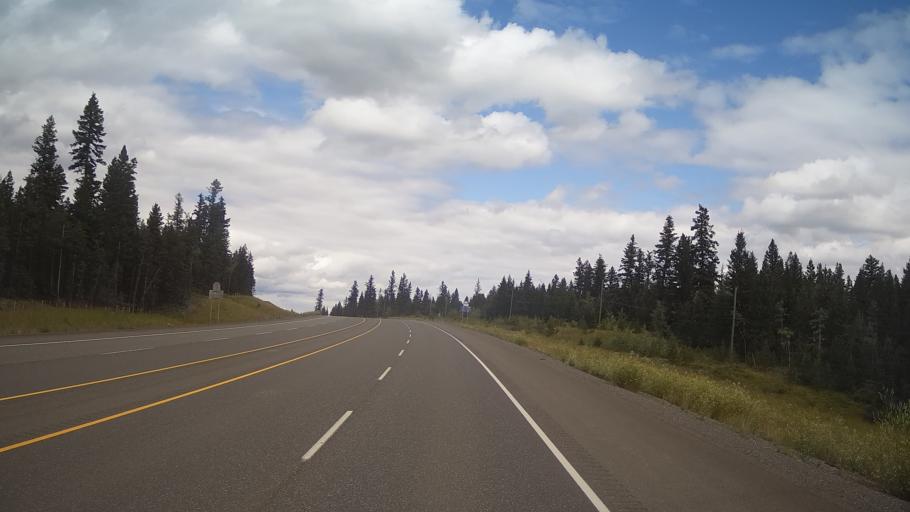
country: CA
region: British Columbia
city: Cache Creek
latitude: 51.3736
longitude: -121.3626
